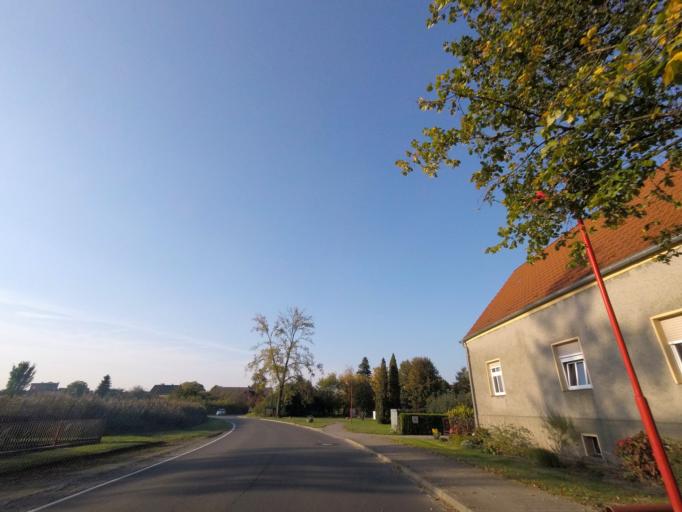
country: DE
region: Saxony-Anhalt
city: Seyda
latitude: 51.9504
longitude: 12.9136
